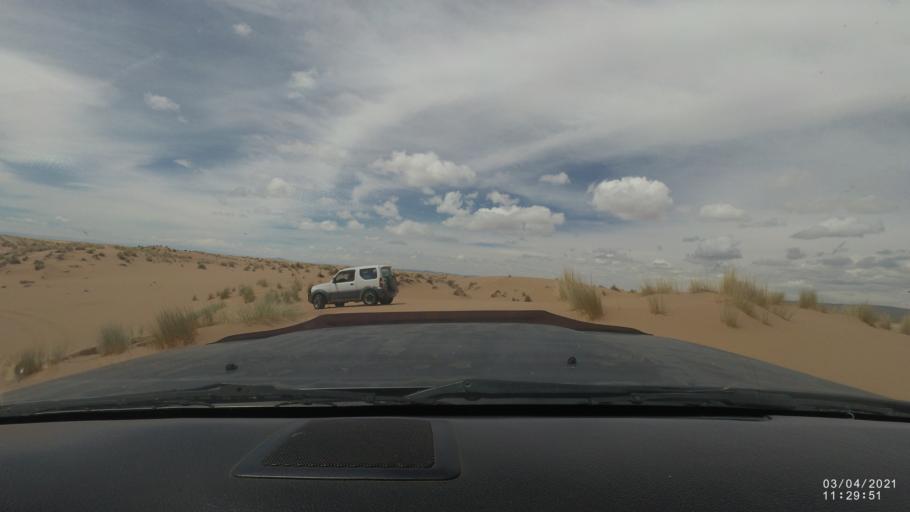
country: BO
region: Oruro
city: Poopo
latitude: -18.7024
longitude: -67.5086
